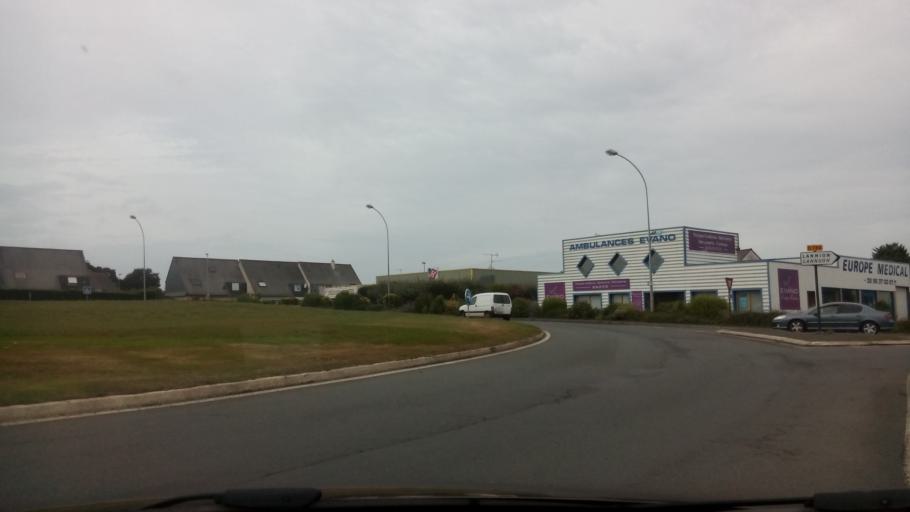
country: FR
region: Brittany
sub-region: Departement des Cotes-d'Armor
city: Lannion
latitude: 48.7219
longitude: -3.4807
